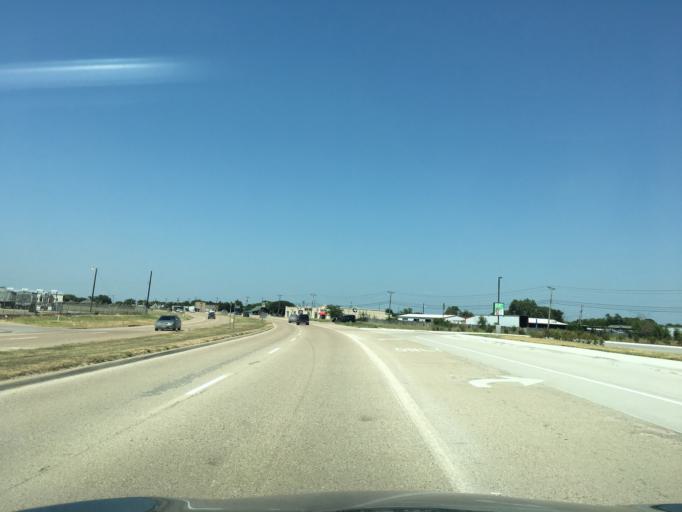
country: US
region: Texas
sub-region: Tarrant County
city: Crowley
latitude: 32.6143
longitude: -97.3496
